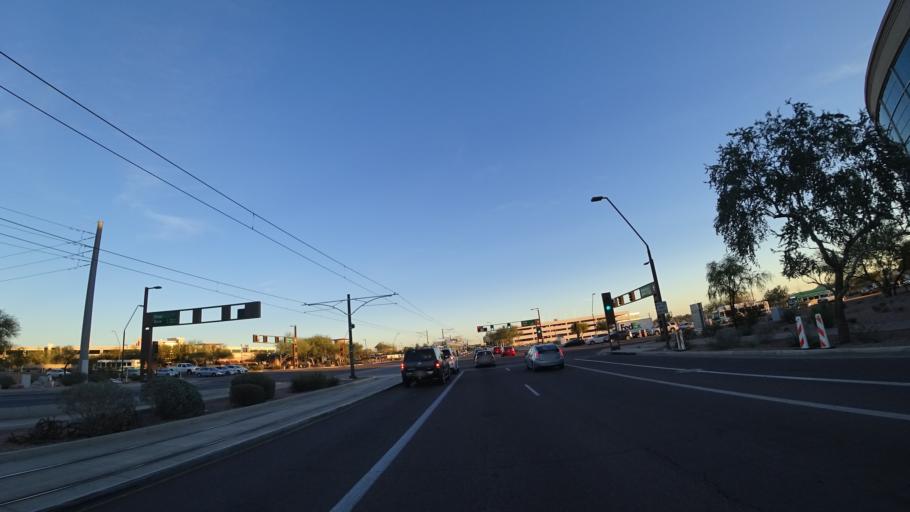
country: US
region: Arizona
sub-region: Maricopa County
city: Tempe Junction
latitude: 33.4430
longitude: -111.9571
